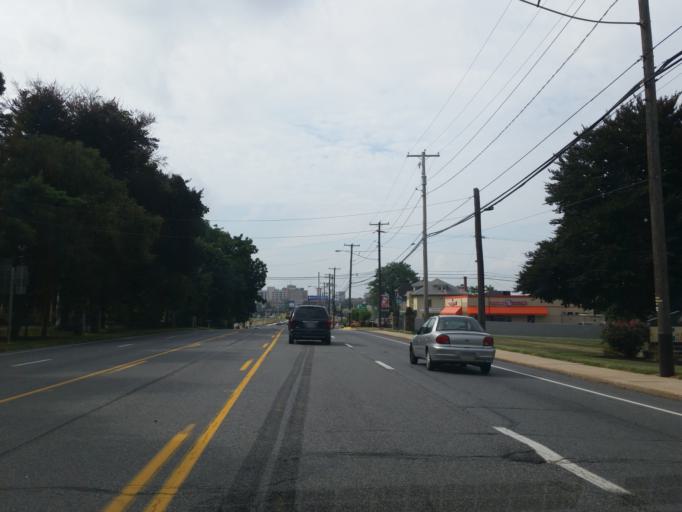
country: US
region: Pennsylvania
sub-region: Lancaster County
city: Lancaster
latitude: 40.0590
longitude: -76.3060
